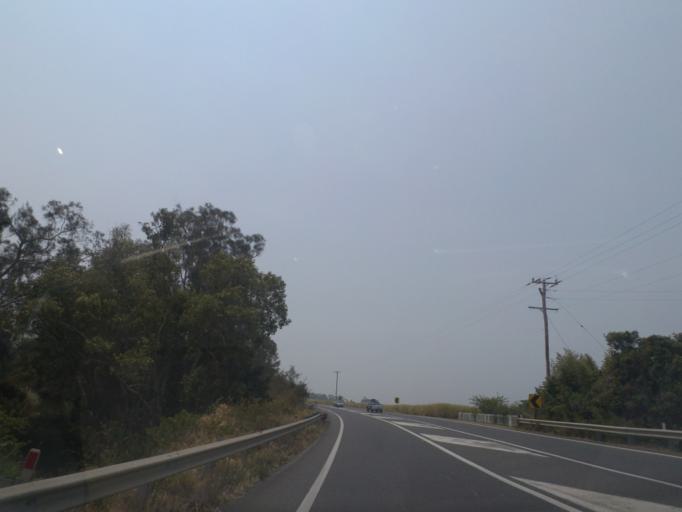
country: AU
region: New South Wales
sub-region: Richmond Valley
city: Evans Head
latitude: -28.9926
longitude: 153.4618
